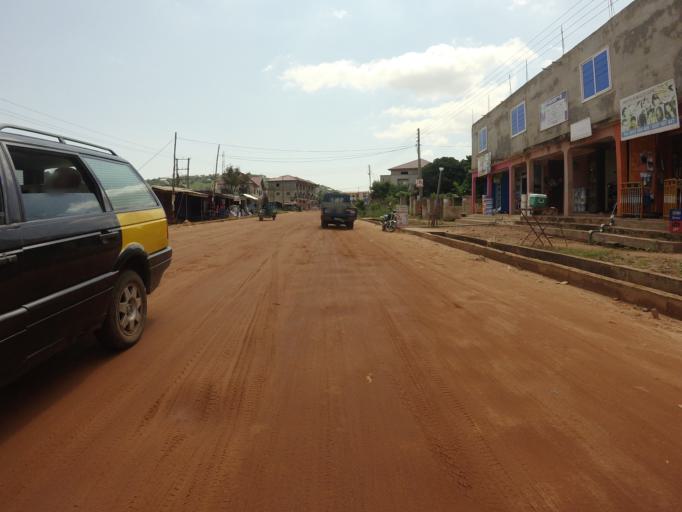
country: GH
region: Greater Accra
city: Gbawe
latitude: 5.6221
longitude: -0.3058
